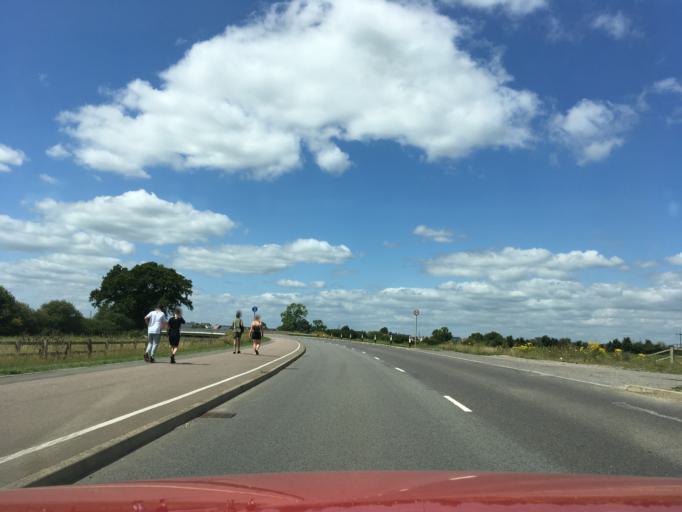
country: GB
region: England
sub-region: Buckinghamshire
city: Aylesbury
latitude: 51.8392
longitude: -0.8406
